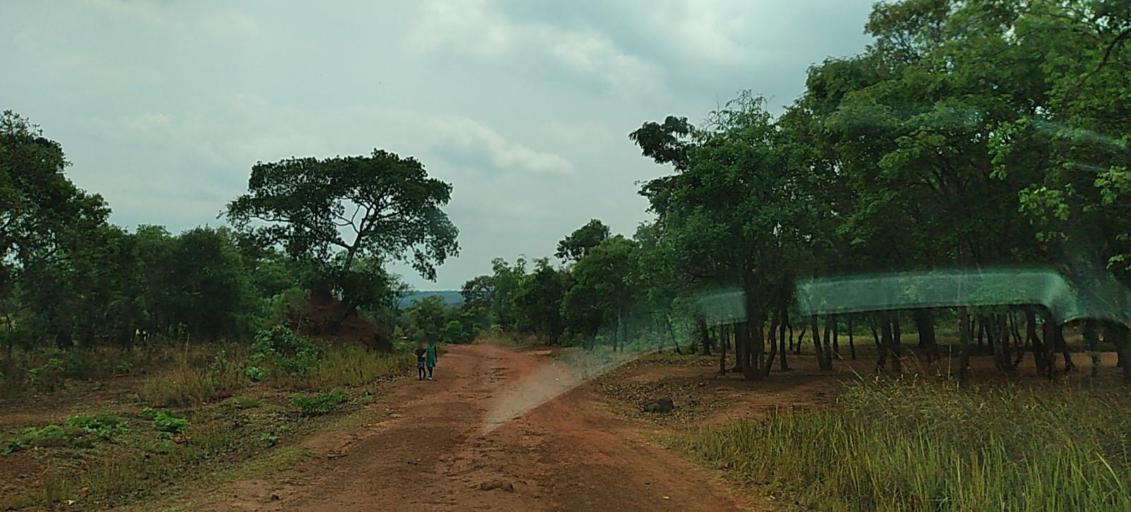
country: ZM
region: North-Western
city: Mwinilunga
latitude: -11.5161
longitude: 24.7896
